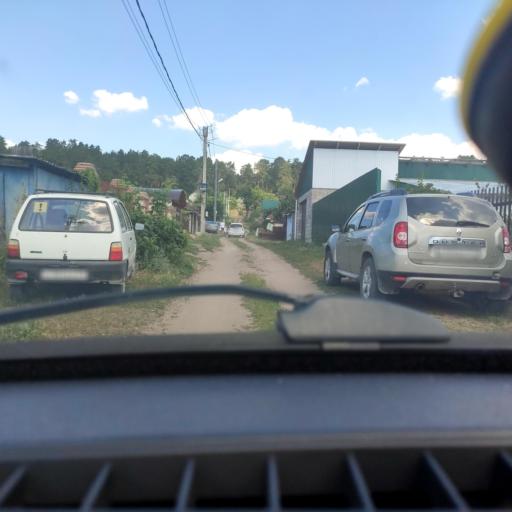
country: RU
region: Samara
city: Zhigulevsk
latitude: 53.4696
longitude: 49.5917
